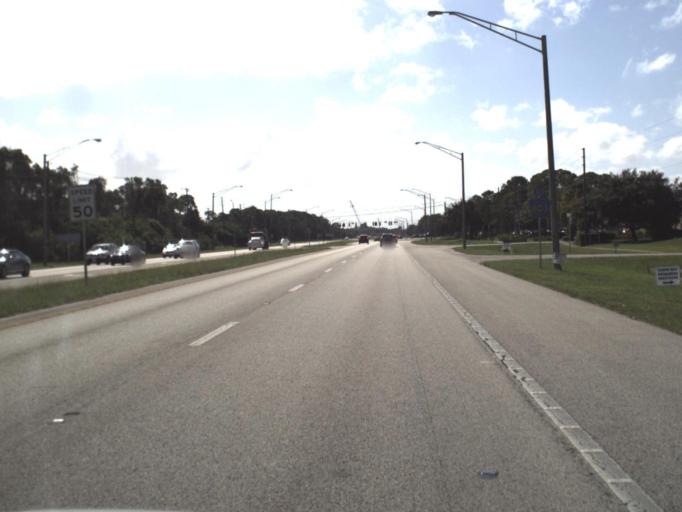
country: US
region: Florida
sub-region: Pinellas County
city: Gandy
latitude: 27.8719
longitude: -82.6499
